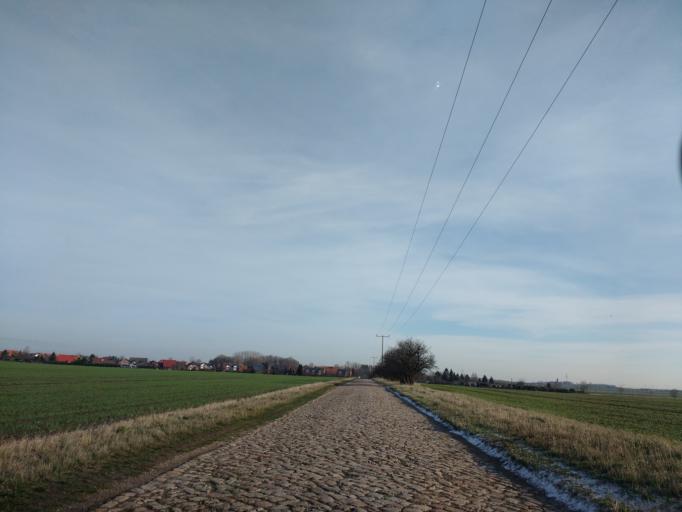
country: DE
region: Saxony-Anhalt
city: Braschwitz
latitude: 51.5349
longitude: 12.0521
